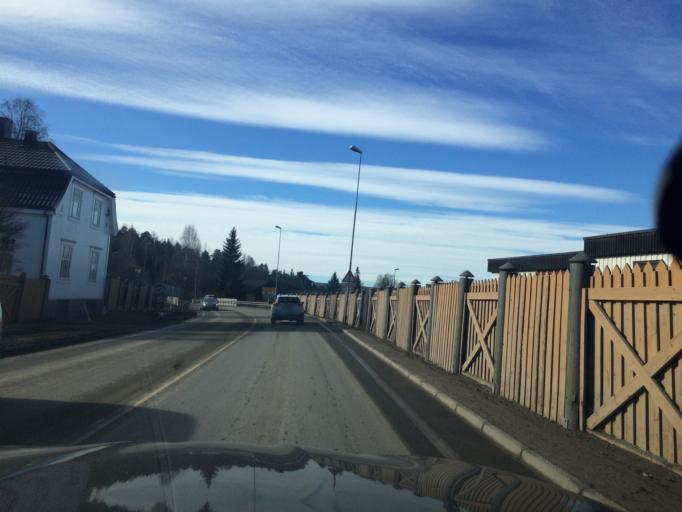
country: NO
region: Hedmark
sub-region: Elverum
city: Elverum
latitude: 60.8872
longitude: 11.5686
